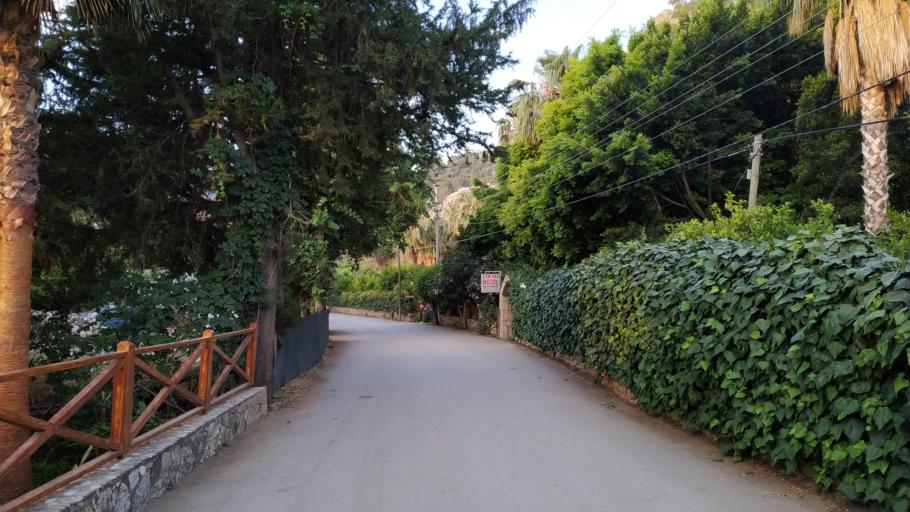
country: TR
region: Antalya
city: Tekirova
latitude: 36.4074
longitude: 30.4750
